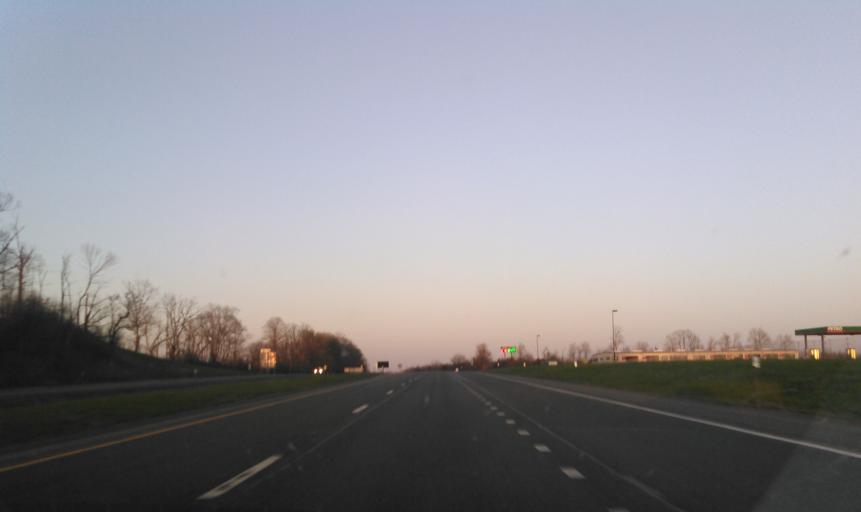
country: US
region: New York
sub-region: Seneca County
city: Waterloo
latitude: 42.9676
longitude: -76.8467
